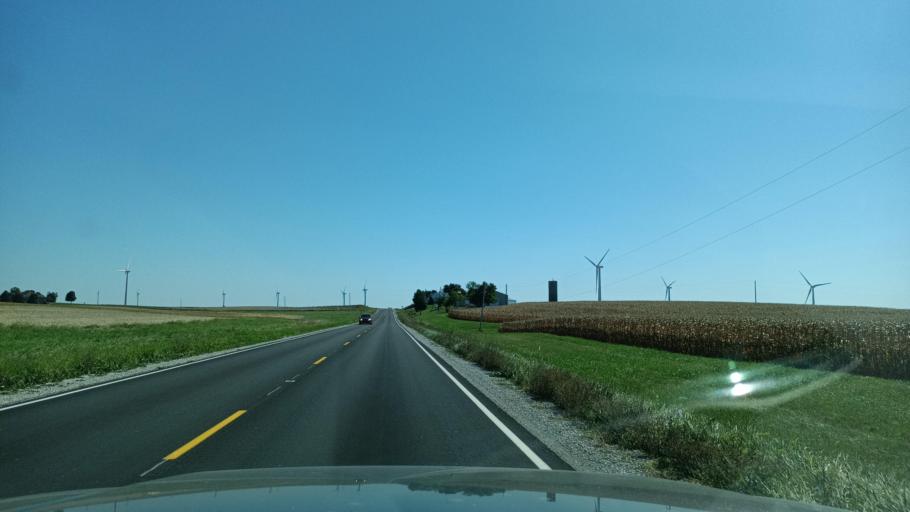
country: US
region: Illinois
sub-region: McLean County
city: Twin Grove
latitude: 40.5709
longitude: -89.0913
